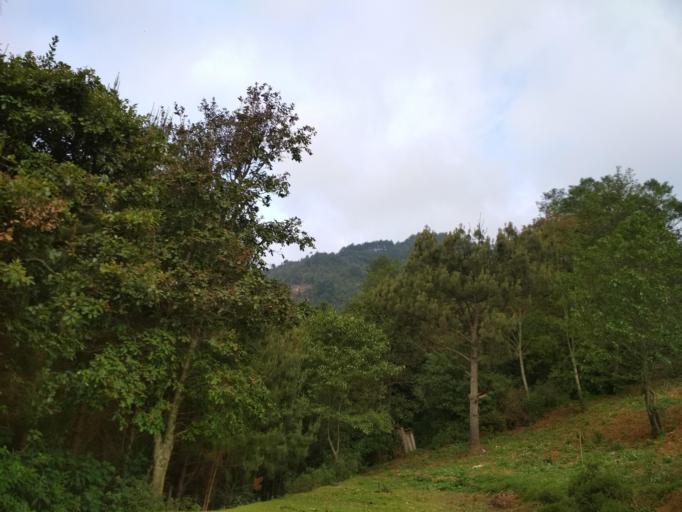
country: MX
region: Veracruz
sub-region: Soledad Atzompa
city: Tlatilpa
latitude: 18.7538
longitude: -97.1580
